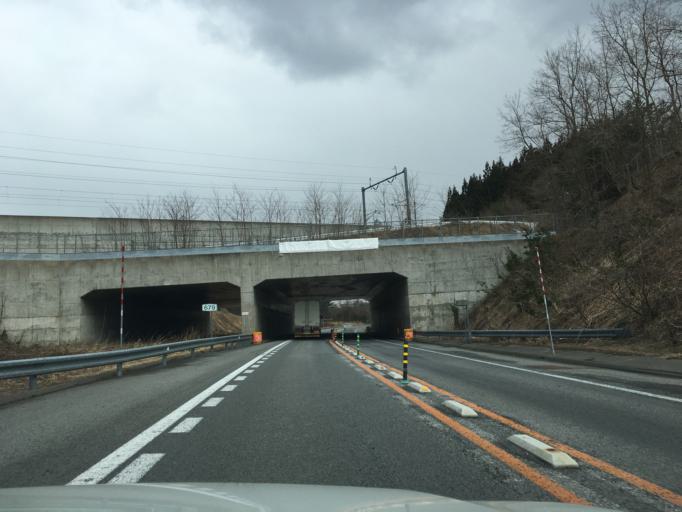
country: JP
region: Aomori
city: Aomori Shi
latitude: 40.8035
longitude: 140.6921
